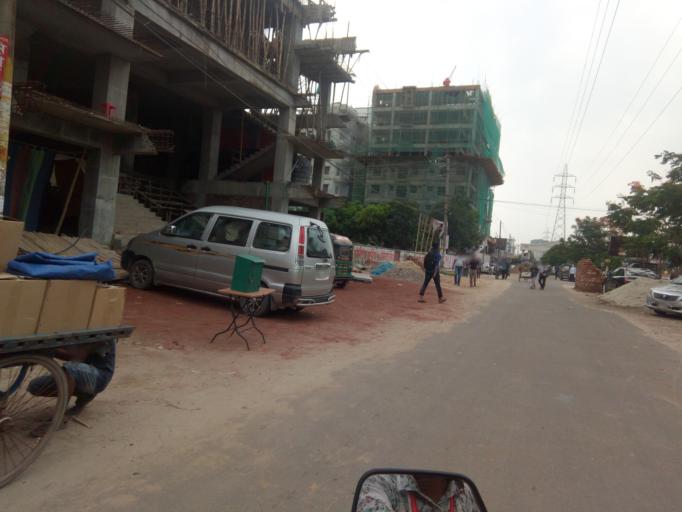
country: BD
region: Dhaka
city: Paltan
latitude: 23.7676
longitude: 90.4262
